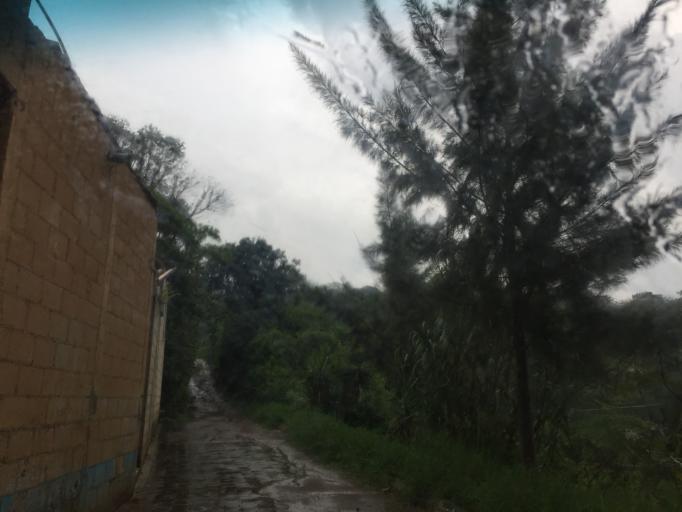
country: GT
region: Guatemala
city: Amatitlan
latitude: 14.5016
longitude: -90.6451
